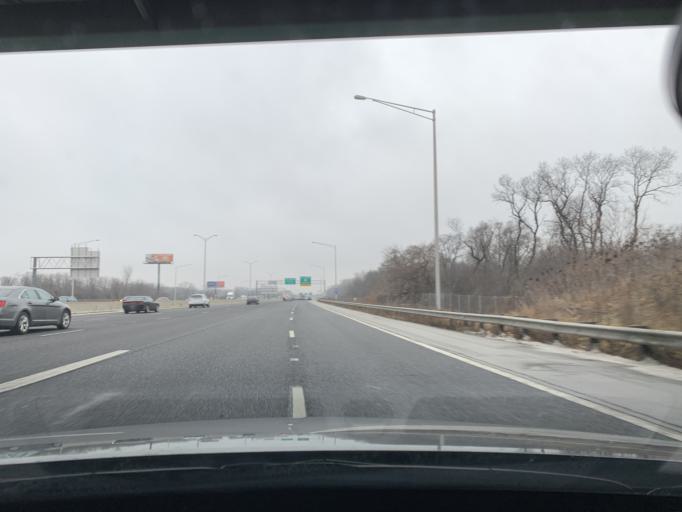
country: US
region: Illinois
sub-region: Cook County
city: Markham
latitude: 41.6117
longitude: -87.6964
